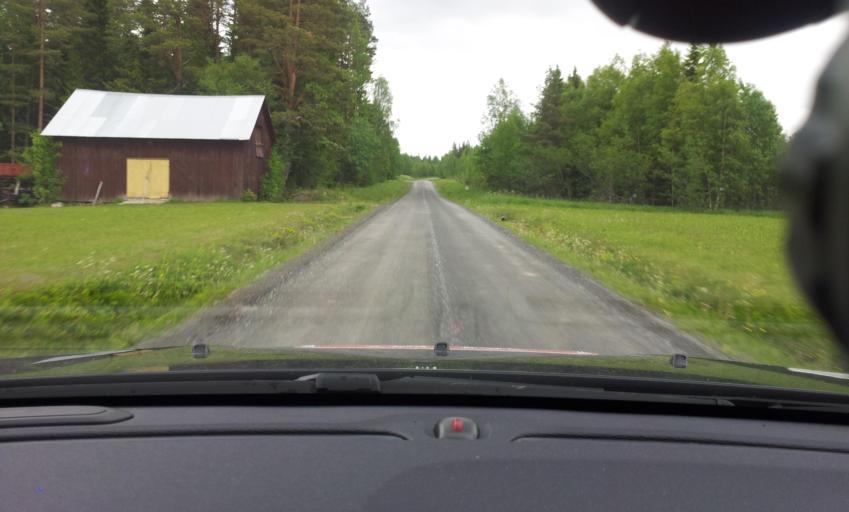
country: SE
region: Jaemtland
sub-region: OEstersunds Kommun
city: Brunflo
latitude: 63.1498
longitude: 15.0259
